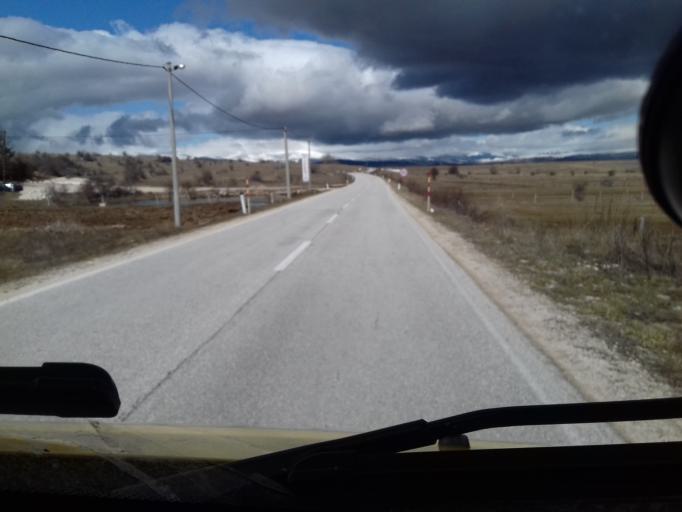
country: BA
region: Federation of Bosnia and Herzegovina
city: Dreznica
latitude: 43.6110
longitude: 17.2682
